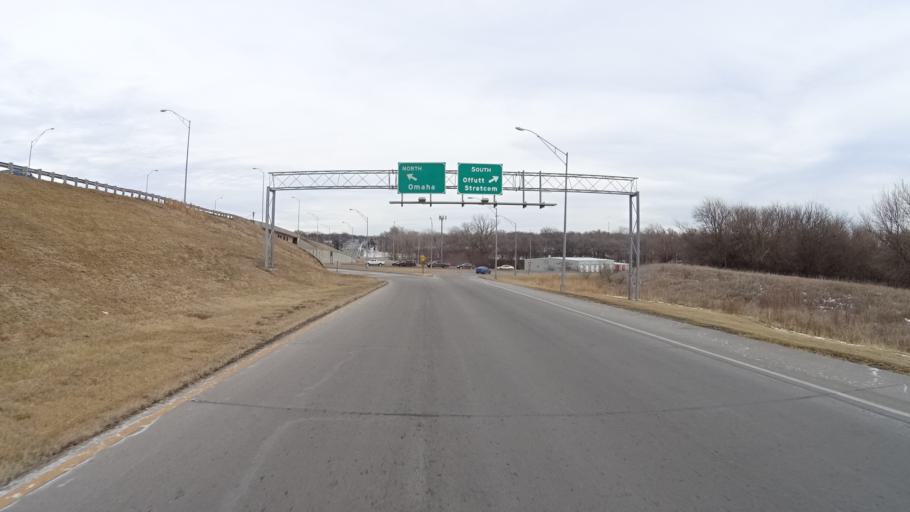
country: US
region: Nebraska
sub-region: Sarpy County
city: Offutt Air Force Base
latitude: 41.1399
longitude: -95.9284
